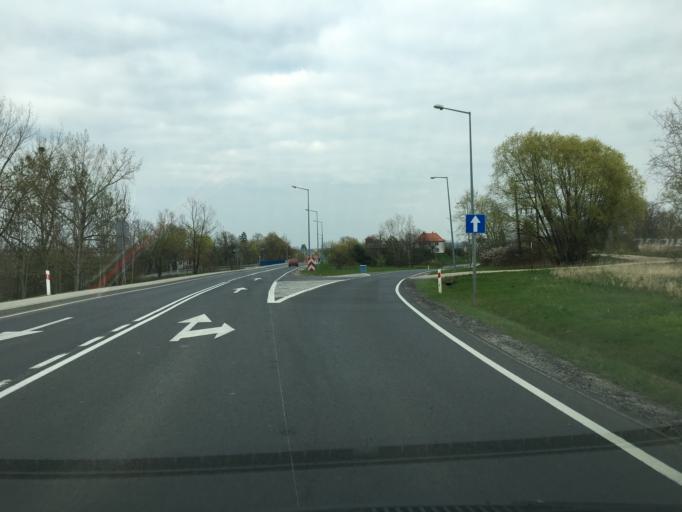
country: PL
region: Lower Silesian Voivodeship
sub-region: Powiat legnicki
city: Prochowice
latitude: 51.2711
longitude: 16.3522
